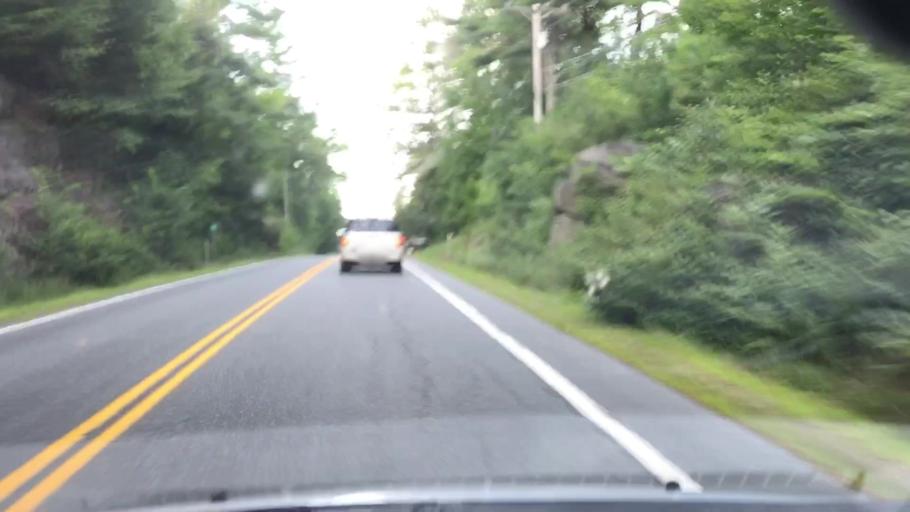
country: US
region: New Hampshire
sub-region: Grafton County
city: Rumney
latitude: 43.8822
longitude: -71.9087
